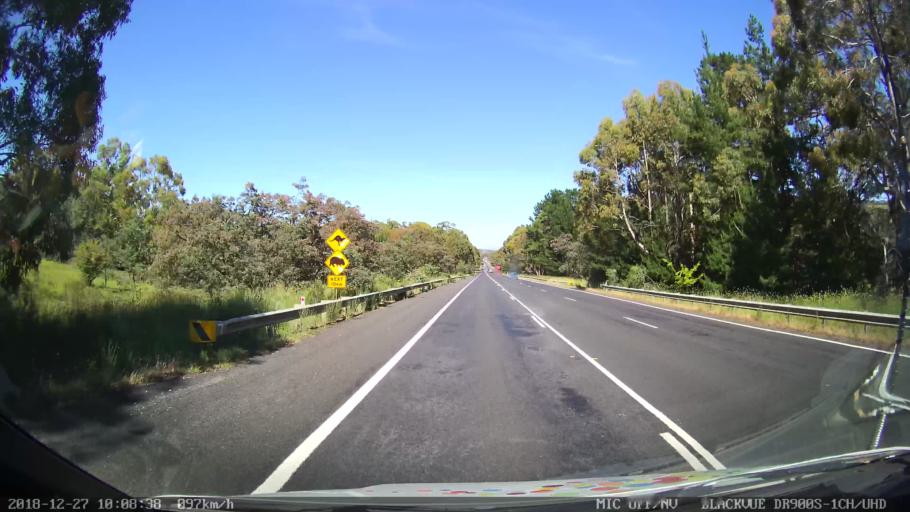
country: AU
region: New South Wales
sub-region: Lithgow
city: Portland
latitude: -33.4486
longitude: 149.8225
